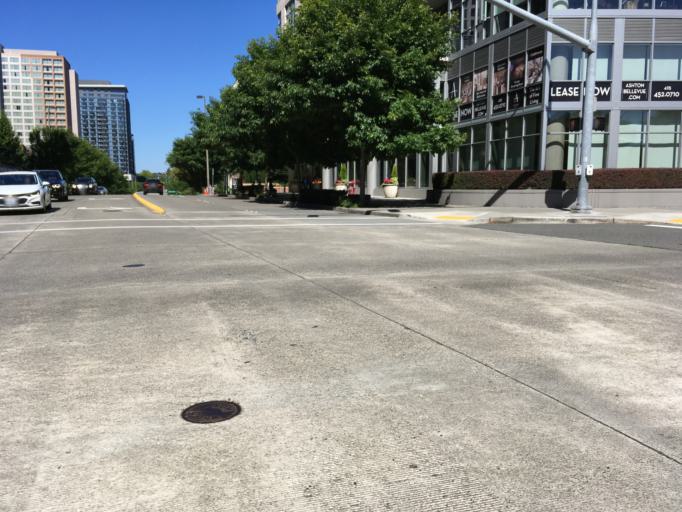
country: US
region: Washington
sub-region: King County
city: Bellevue
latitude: 47.6192
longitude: -122.1963
